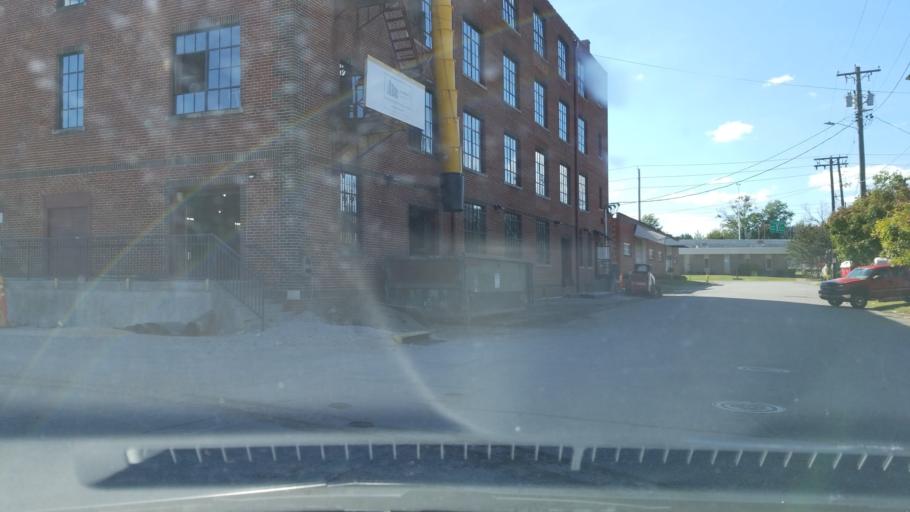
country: US
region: Tennessee
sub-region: Hamilton County
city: Chattanooga
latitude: 35.0398
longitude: -85.3137
